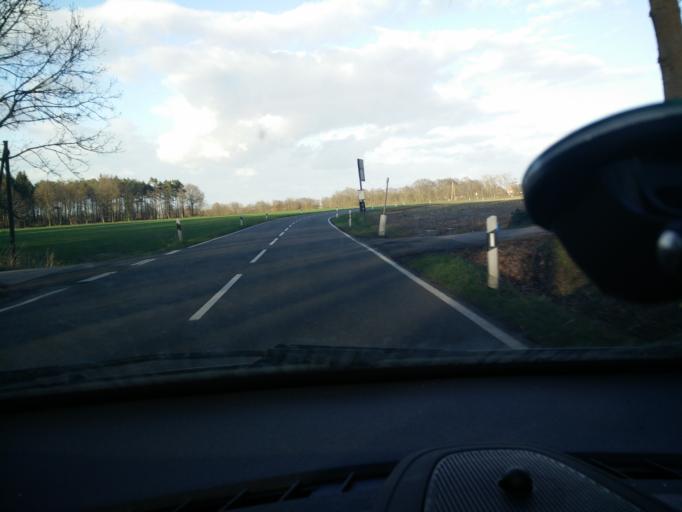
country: DE
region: North Rhine-Westphalia
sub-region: Regierungsbezirk Munster
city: Raesfeld
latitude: 51.7788
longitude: 6.8746
